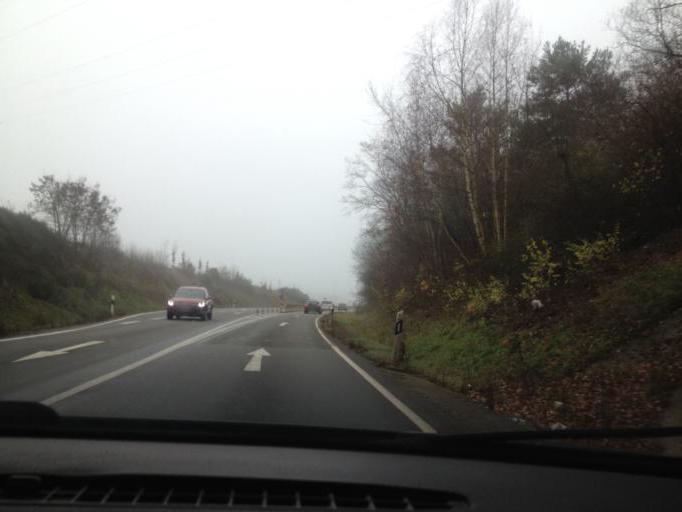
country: DE
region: Rheinland-Pfalz
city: Katzweiler
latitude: 49.4728
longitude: 7.6986
